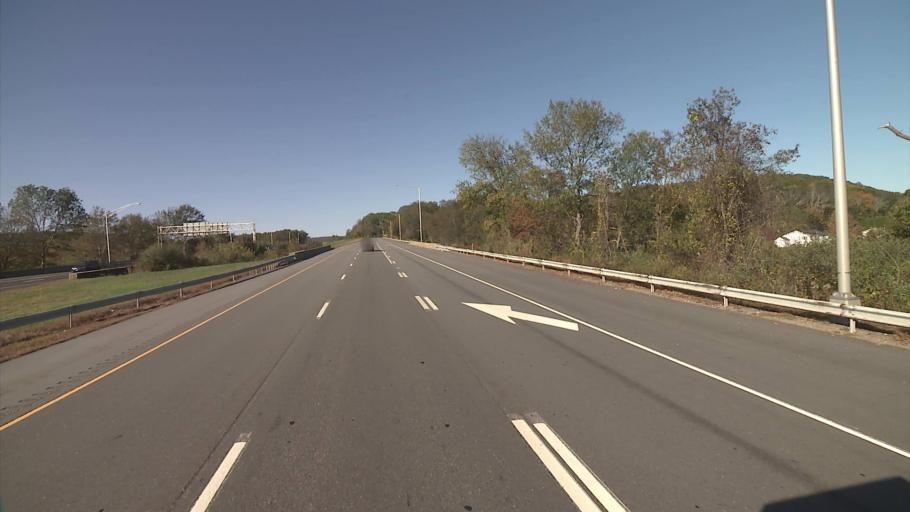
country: US
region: Connecticut
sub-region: Tolland County
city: Mansfield City
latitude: 41.7238
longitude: -72.2548
